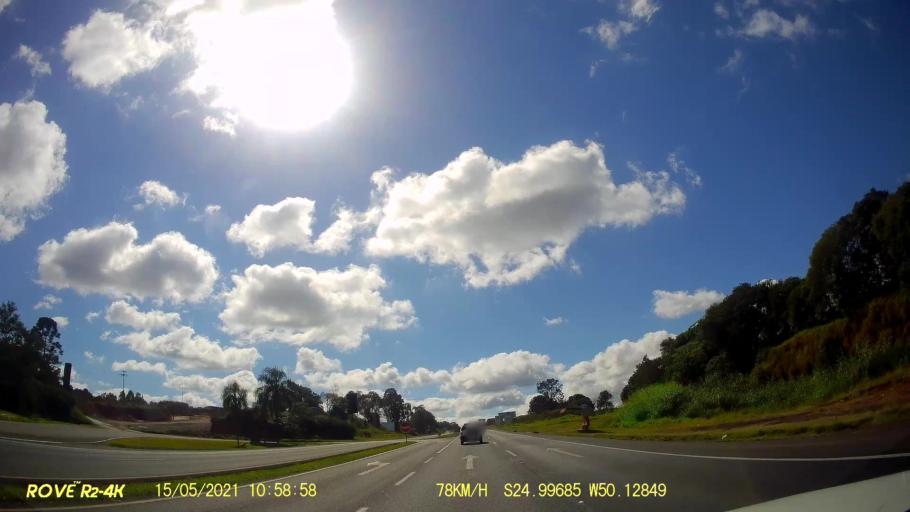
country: BR
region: Parana
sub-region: Carambei
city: Carambei
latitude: -24.9969
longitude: -50.1284
